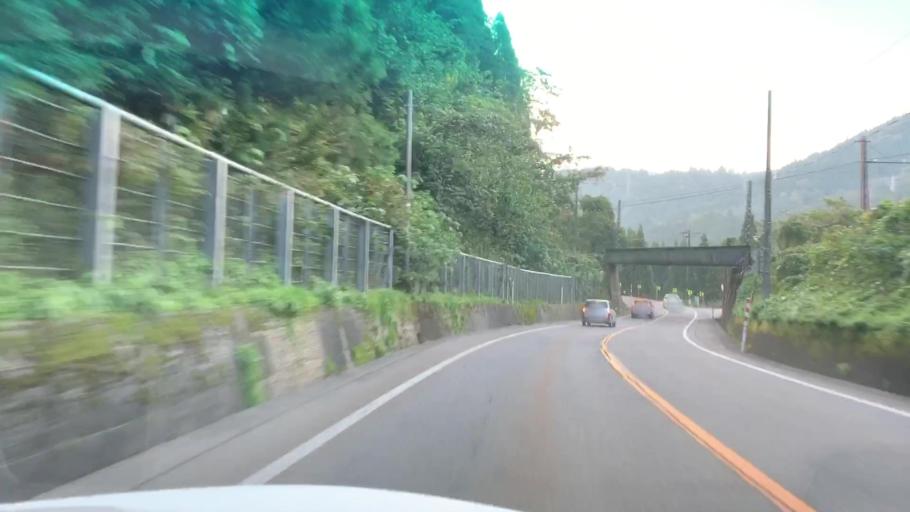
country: JP
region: Toyama
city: Kamiichi
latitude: 36.5758
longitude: 137.3444
